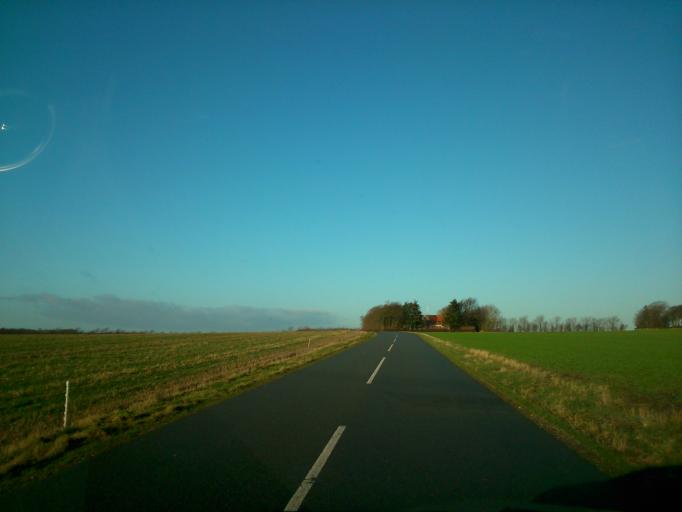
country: DK
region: Central Jutland
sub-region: Ringkobing-Skjern Kommune
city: Skjern
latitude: 55.9744
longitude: 8.5529
